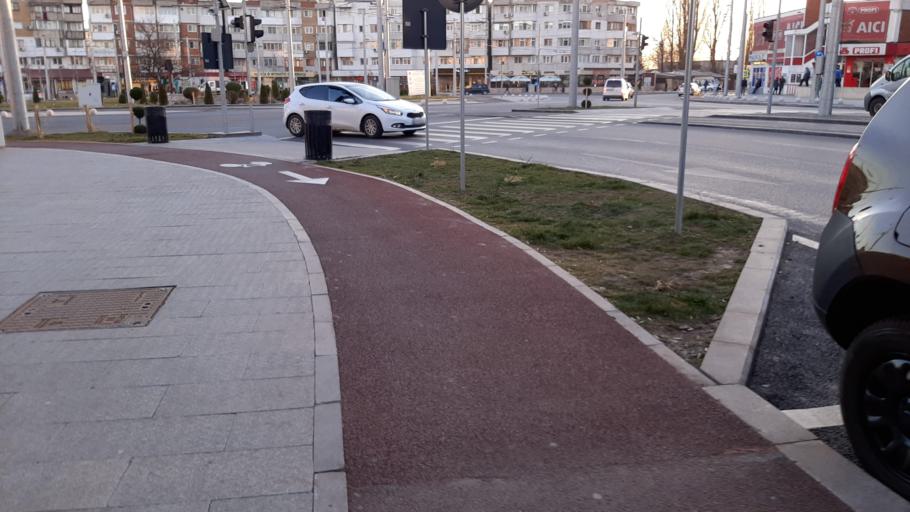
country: RO
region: Galati
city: Galati
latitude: 45.4409
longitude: 28.0210
